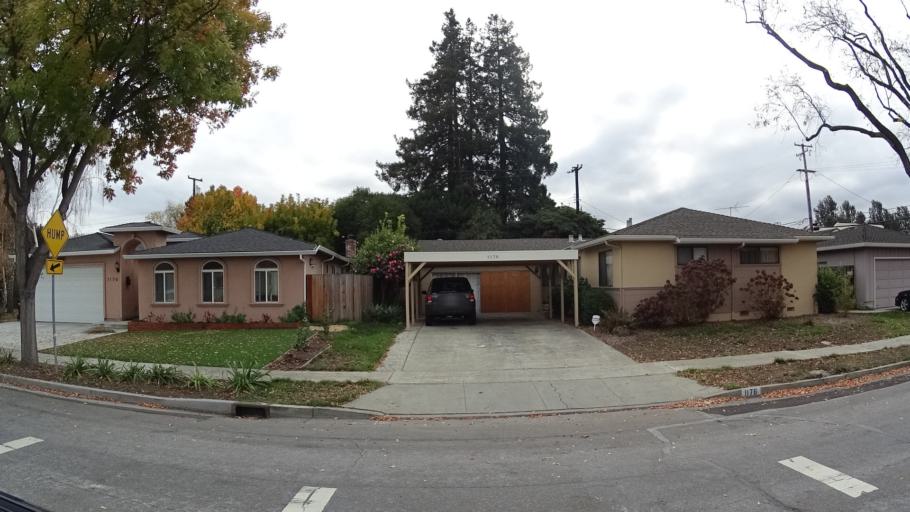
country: US
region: California
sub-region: Santa Clara County
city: Sunnyvale
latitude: 37.3720
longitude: -122.0560
